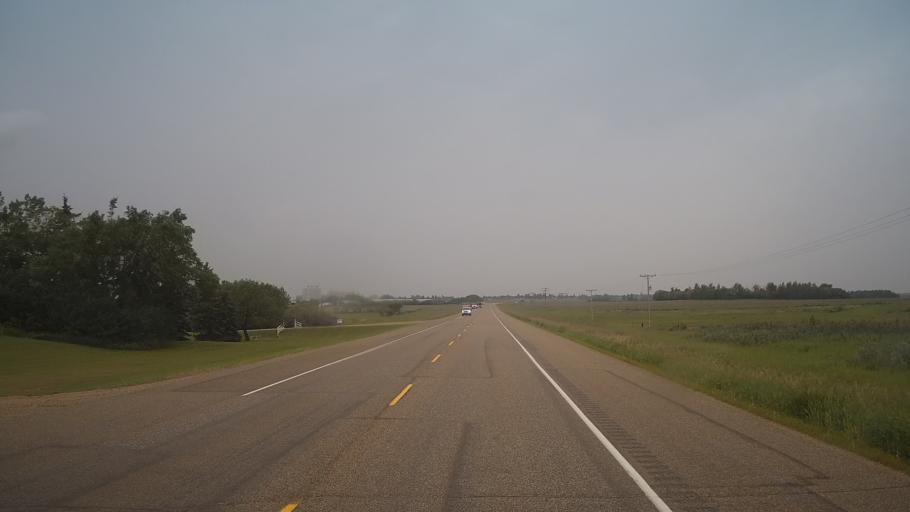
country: CA
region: Saskatchewan
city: Biggar
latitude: 52.0563
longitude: -107.9378
